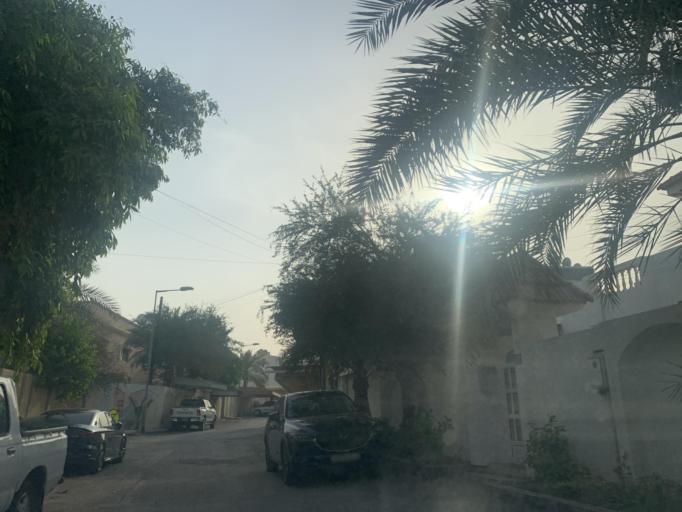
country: BH
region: Northern
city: Ar Rifa'
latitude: 26.1333
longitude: 50.5563
